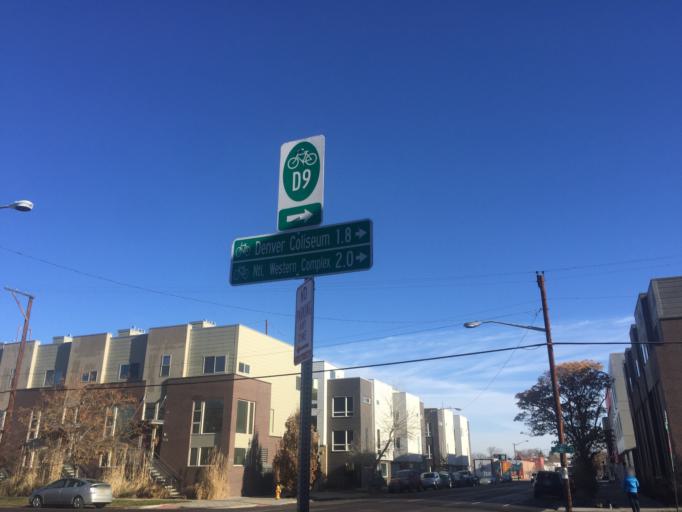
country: US
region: Colorado
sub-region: Denver County
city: Denver
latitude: 39.7657
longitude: -104.9758
